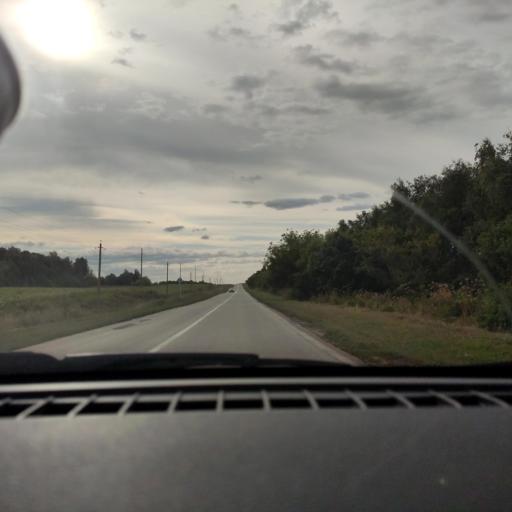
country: RU
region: Samara
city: Georgiyevka
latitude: 53.4283
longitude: 50.7957
